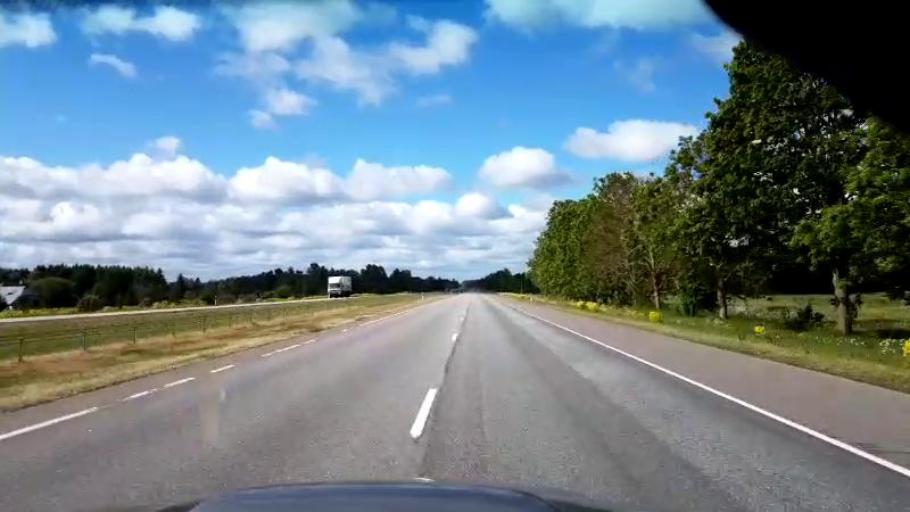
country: EE
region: Harju
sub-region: Saue linn
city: Saue
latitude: 59.2955
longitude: 24.5490
